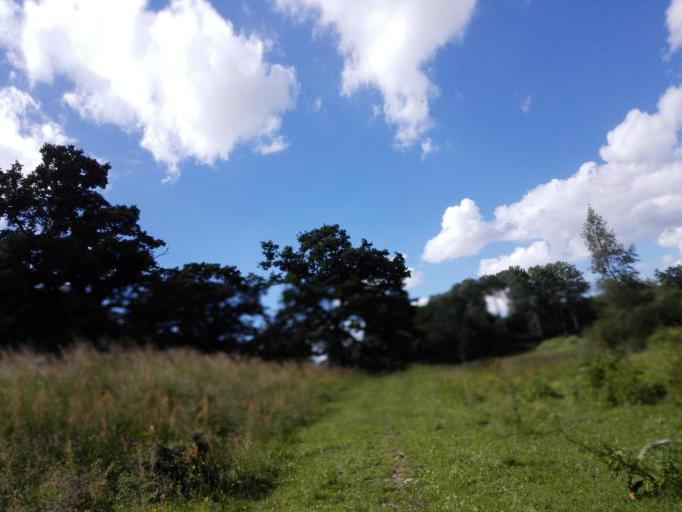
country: DK
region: Capital Region
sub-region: Allerod Kommune
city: Lynge
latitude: 55.8189
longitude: 12.2993
